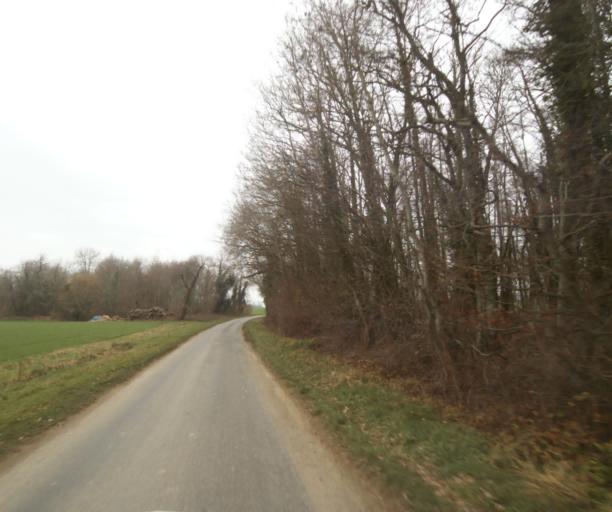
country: FR
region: Champagne-Ardenne
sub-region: Departement de la Haute-Marne
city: Villiers-en-Lieu
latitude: 48.6344
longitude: 4.8114
